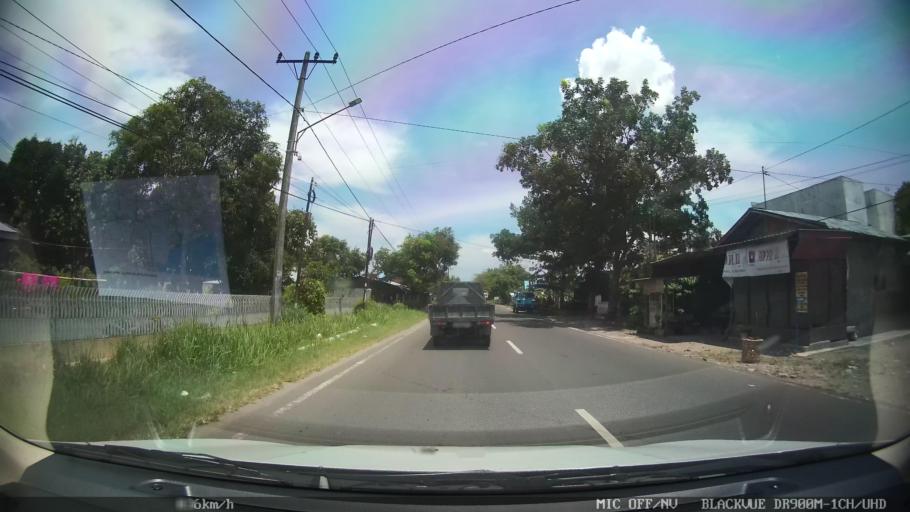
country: ID
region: North Sumatra
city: Binjai
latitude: 3.5961
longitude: 98.5008
